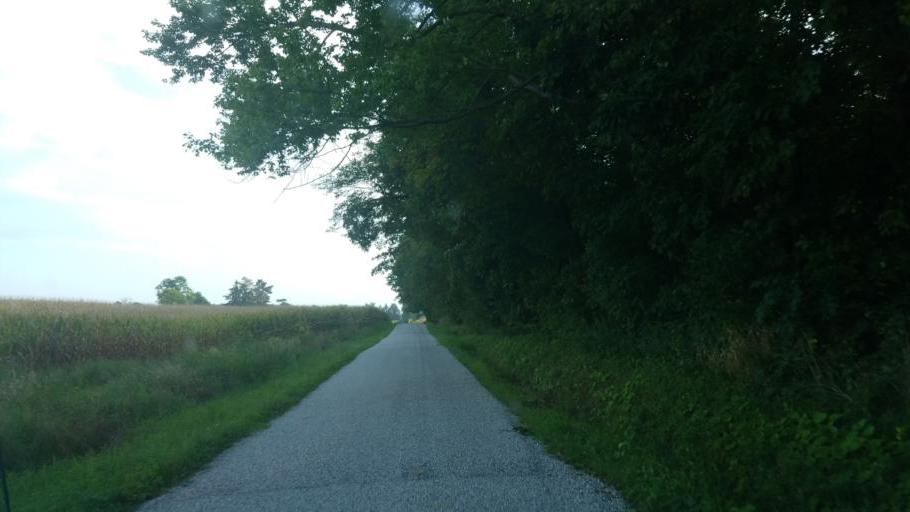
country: US
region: Ohio
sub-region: Wayne County
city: Wooster
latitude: 40.8048
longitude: -82.0422
